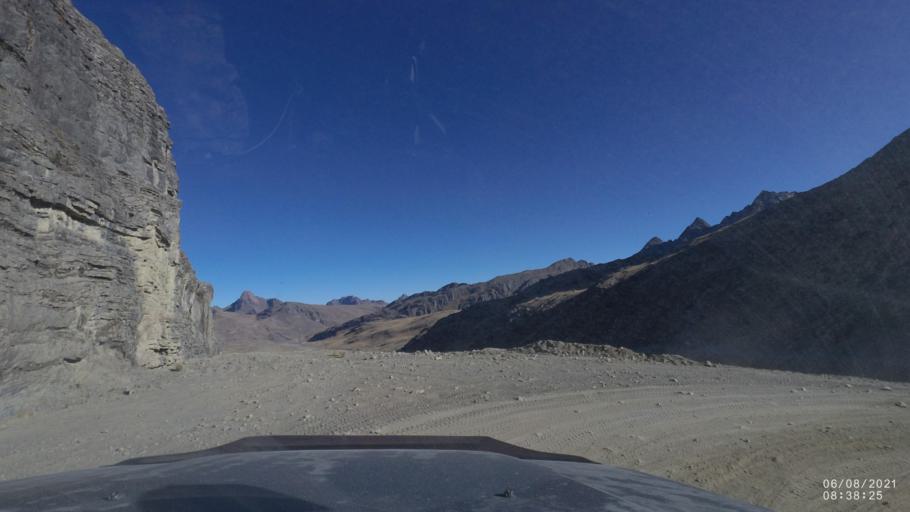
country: BO
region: Cochabamba
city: Sipe Sipe
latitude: -17.1732
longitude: -66.3951
